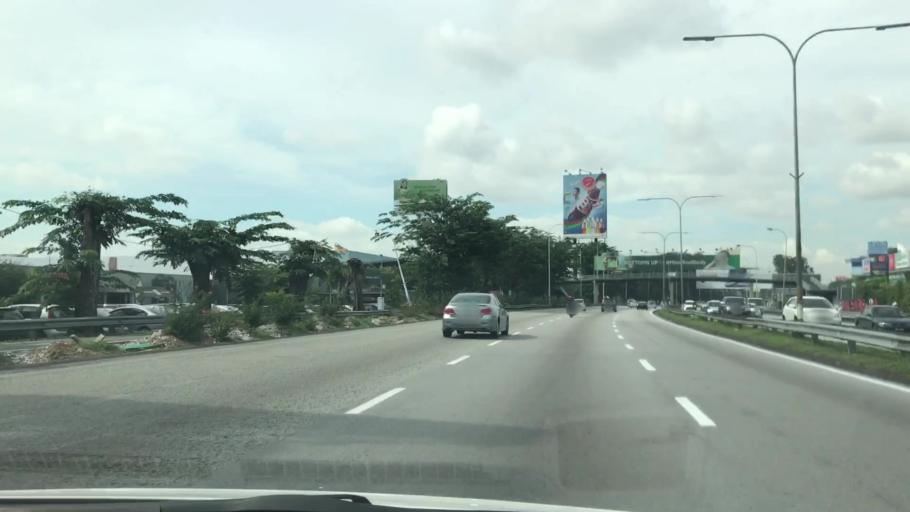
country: MY
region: Selangor
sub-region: Petaling
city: Petaling Jaya
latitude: 3.0932
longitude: 101.6334
